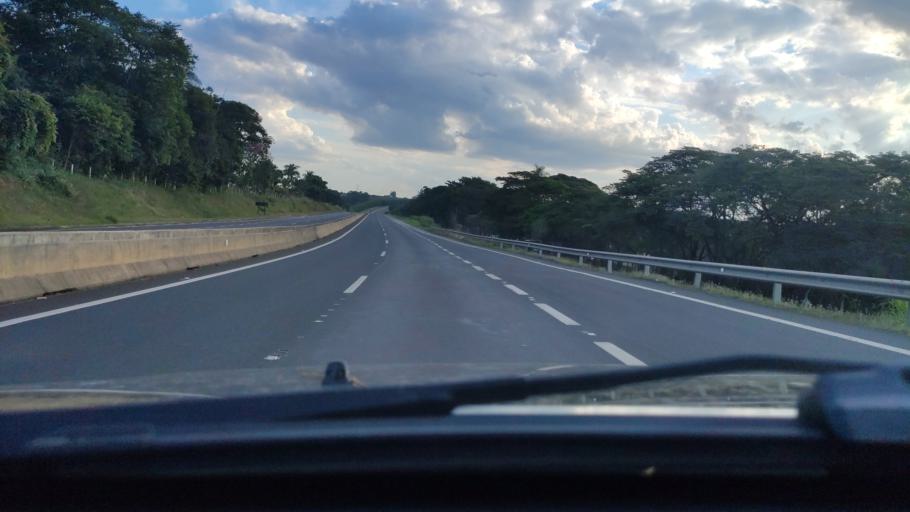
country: BR
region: Sao Paulo
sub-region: Mogi-Mirim
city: Mogi Mirim
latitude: -22.4428
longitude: -47.0519
